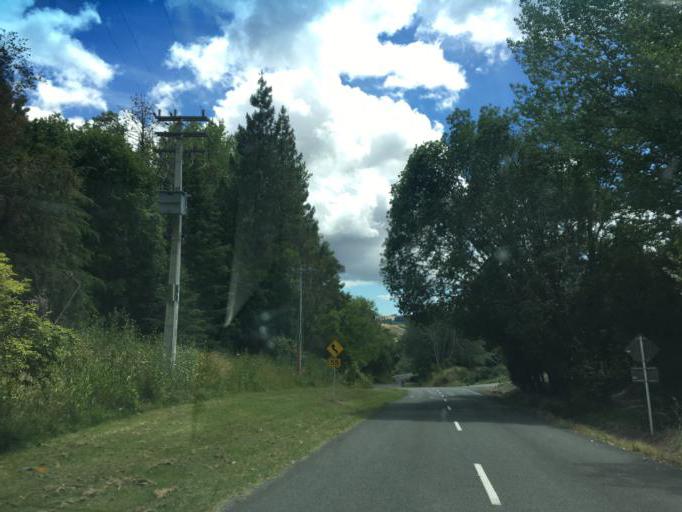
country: NZ
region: Hawke's Bay
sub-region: Hastings District
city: Hastings
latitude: -39.7374
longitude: 176.8973
